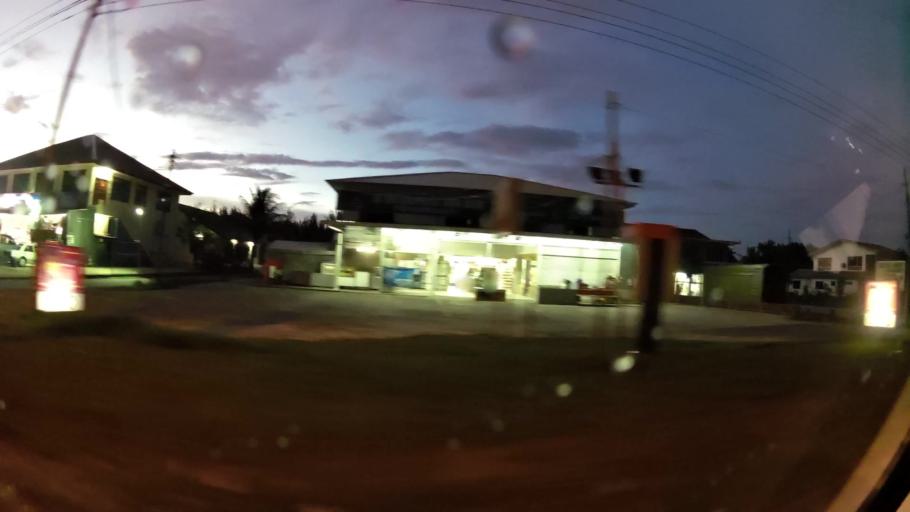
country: BN
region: Belait
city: Seria
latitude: 4.6576
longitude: 114.4384
